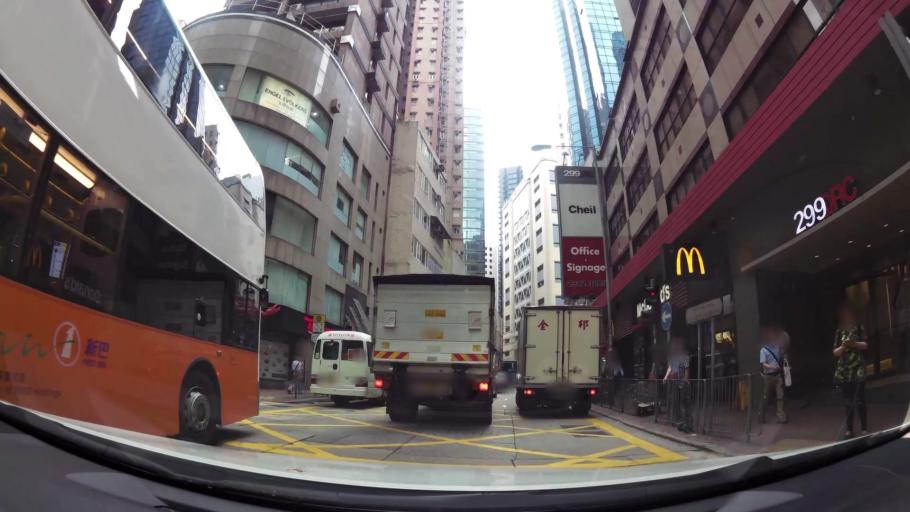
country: HK
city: Hong Kong
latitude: 22.2850
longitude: 114.1506
